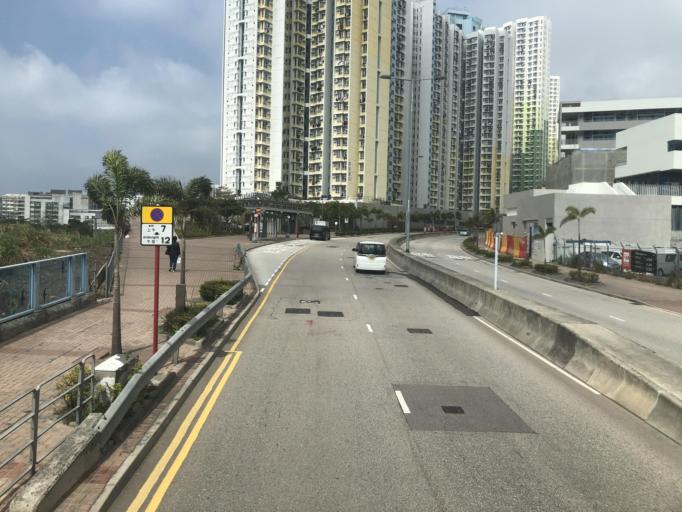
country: HK
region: Kowloon City
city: Kowloon
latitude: 22.3239
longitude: 114.2311
